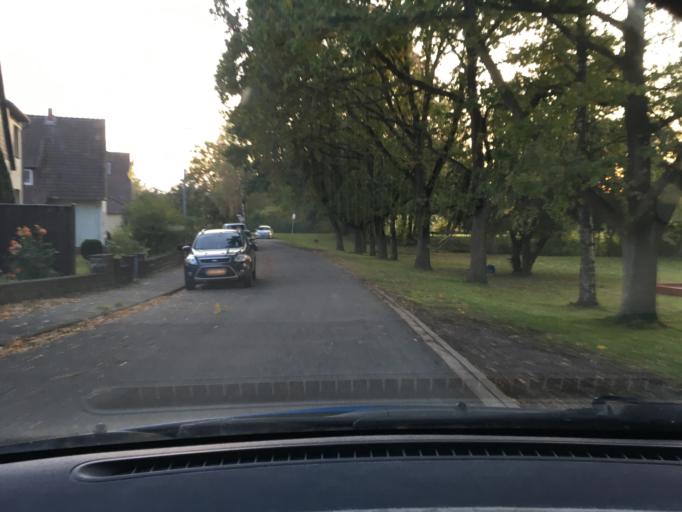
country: DE
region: Lower Saxony
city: Bad Munder am Deister
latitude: 52.2071
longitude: 9.4625
